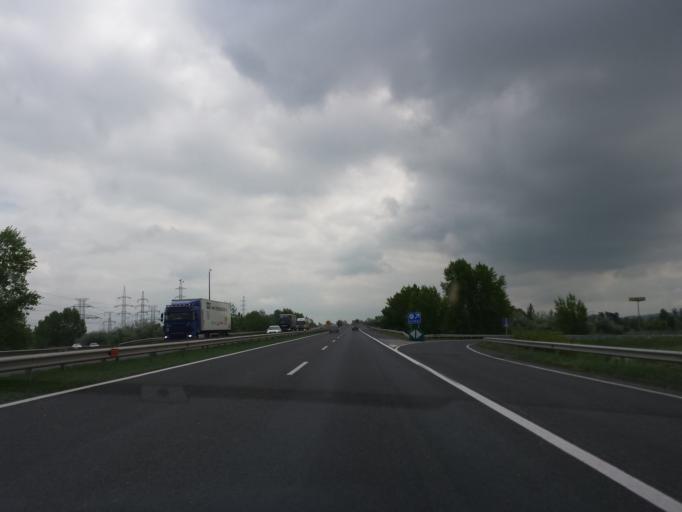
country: HU
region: Gyor-Moson-Sopron
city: Gyor
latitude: 47.6468
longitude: 17.6132
